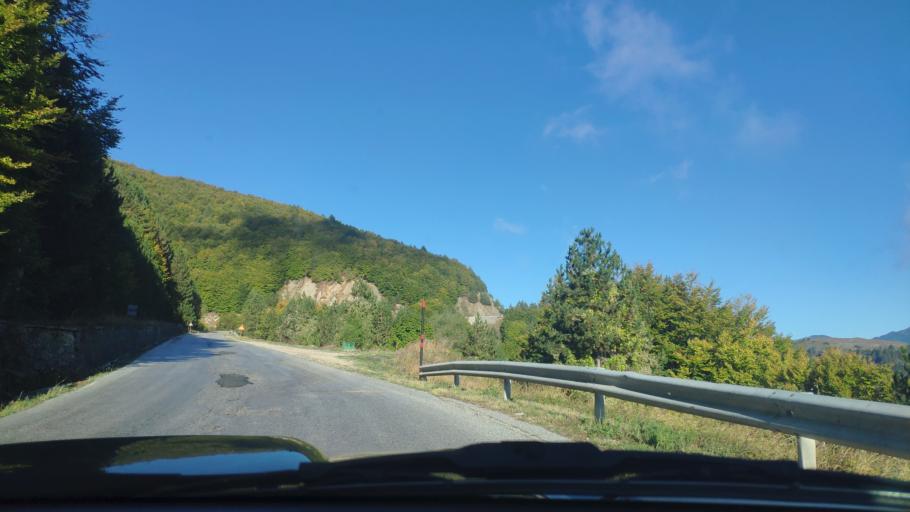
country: GR
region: Epirus
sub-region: Nomos Ioanninon
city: Metsovo
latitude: 39.7771
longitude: 21.1747
